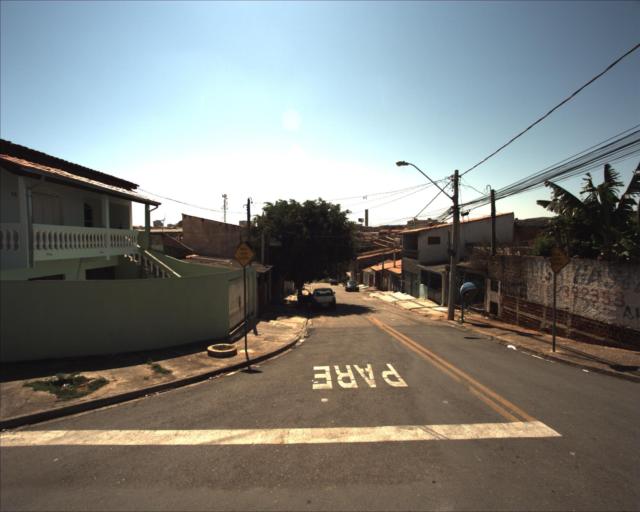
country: BR
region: Sao Paulo
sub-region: Sorocaba
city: Sorocaba
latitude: -23.4667
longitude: -47.4822
